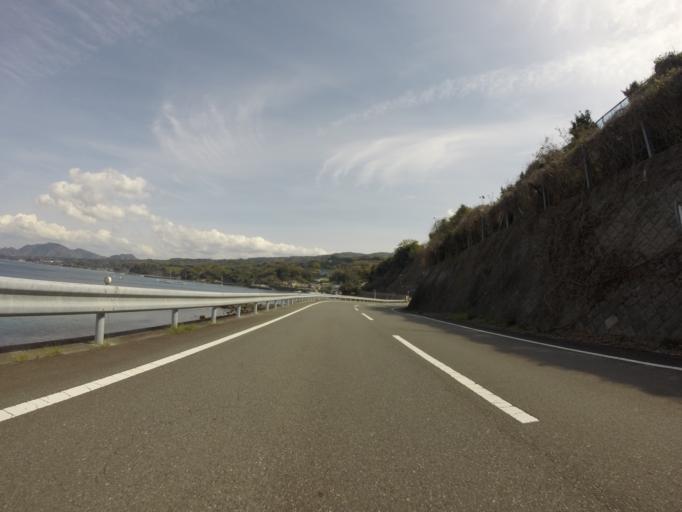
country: JP
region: Shizuoka
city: Heda
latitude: 35.0229
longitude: 138.8293
